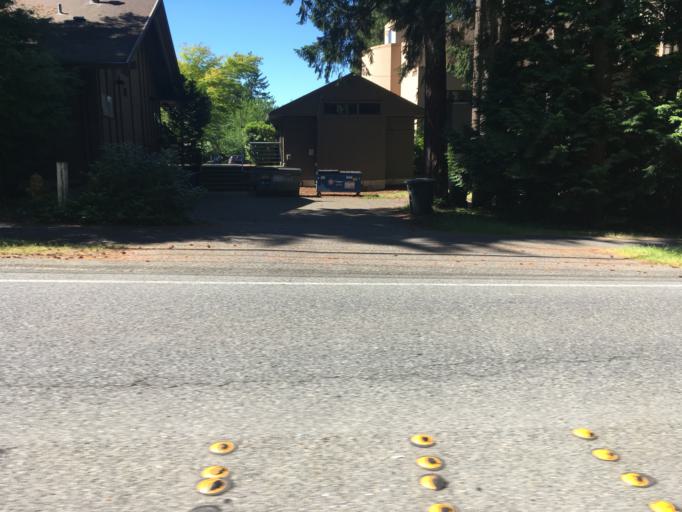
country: US
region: Washington
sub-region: King County
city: Redmond
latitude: 47.6275
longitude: -122.1310
